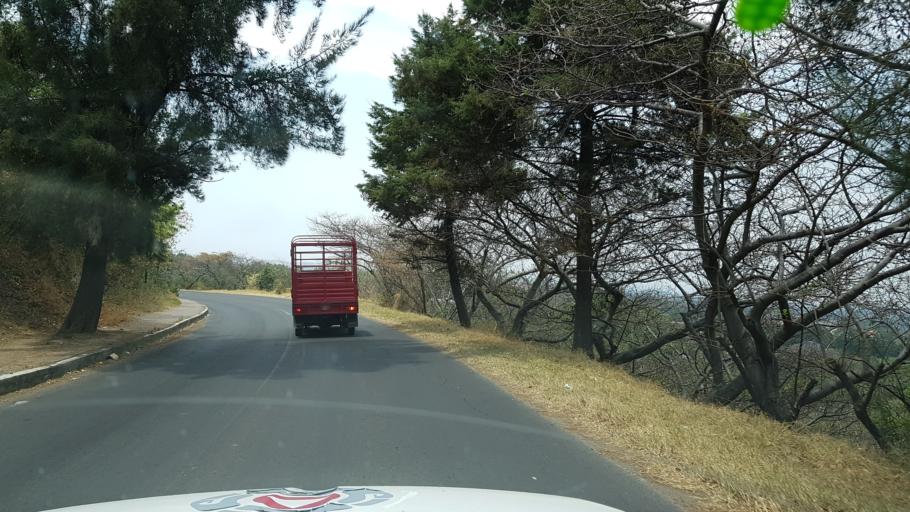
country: MX
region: Morelos
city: Ocuituco
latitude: 18.8813
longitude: -98.7770
